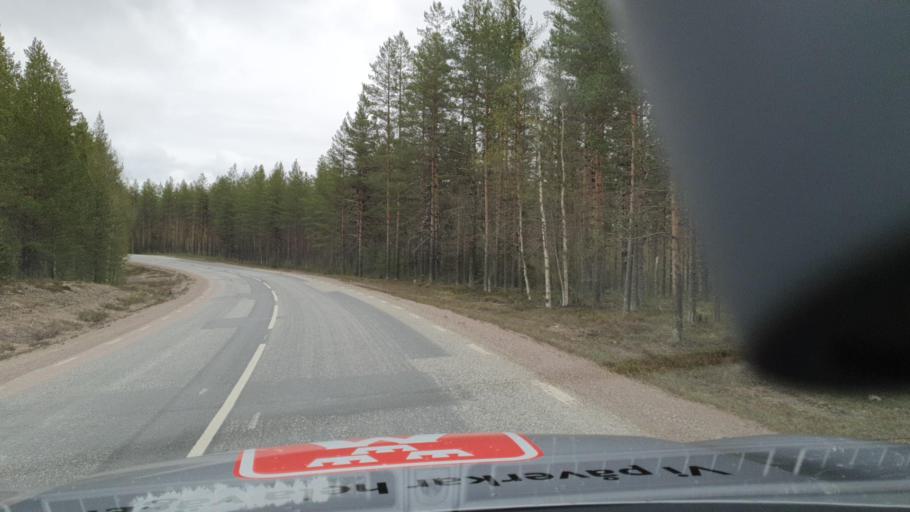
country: SE
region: Vaesternorrland
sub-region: Solleftea Kommun
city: Solleftea
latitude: 63.6413
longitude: 17.4030
